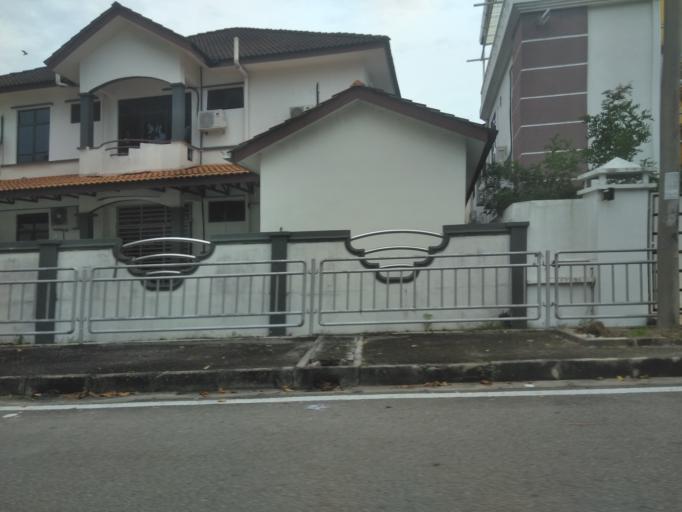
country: MY
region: Penang
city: Bukit Mertajam
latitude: 5.3337
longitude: 100.4805
